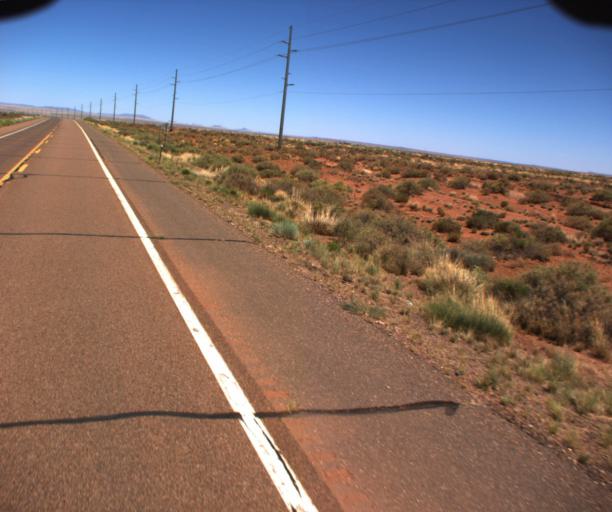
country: US
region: Arizona
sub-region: Coconino County
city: LeChee
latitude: 34.9639
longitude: -110.7385
